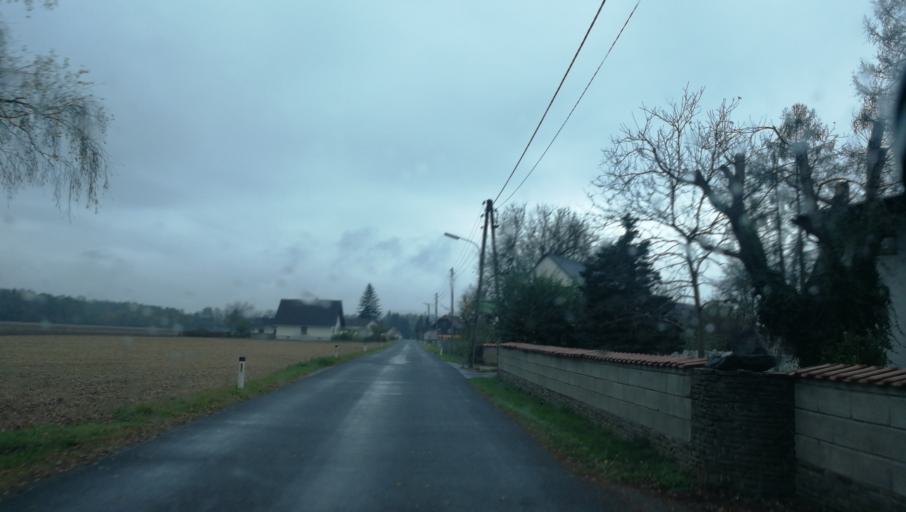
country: AT
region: Styria
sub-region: Politischer Bezirk Leibnitz
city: Sankt Veit am Vogau
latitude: 46.7443
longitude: 15.6235
